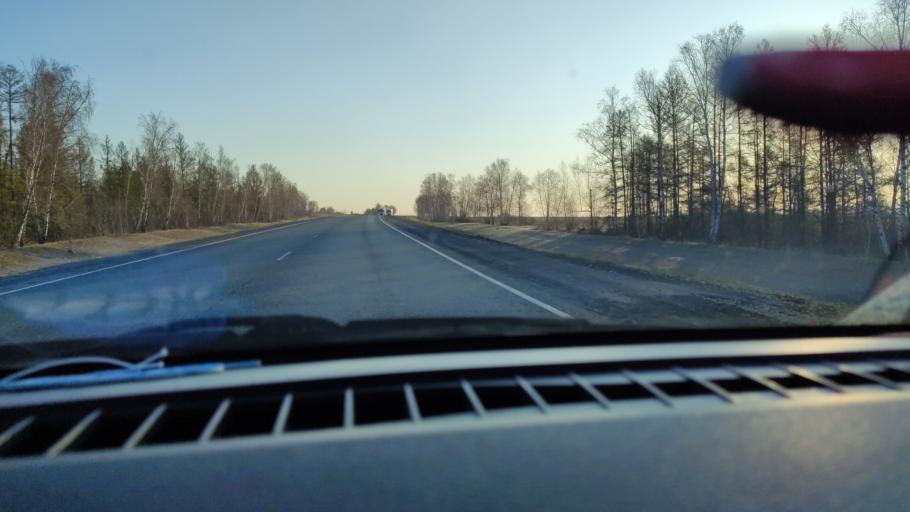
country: RU
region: Saratov
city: Sennoy
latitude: 52.1316
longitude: 46.8630
